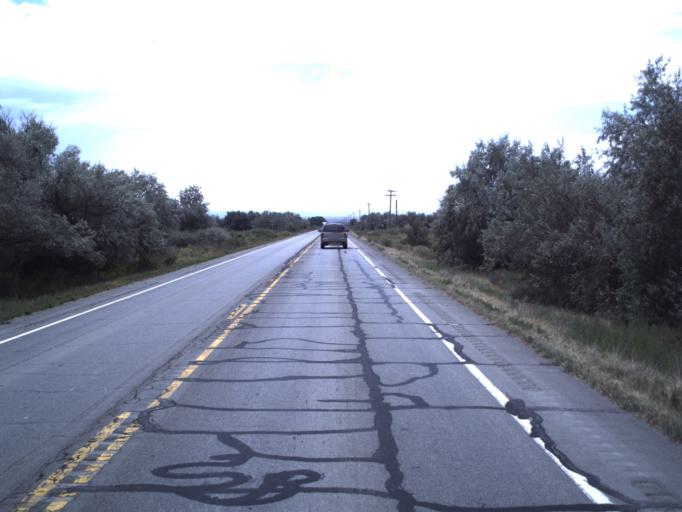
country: US
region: Utah
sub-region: Duchesne County
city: Roosevelt
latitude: 40.1769
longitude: -110.1218
